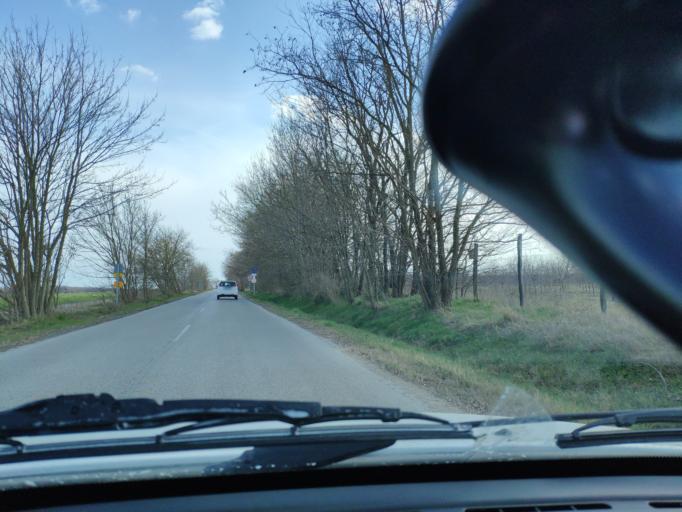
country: HU
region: Pest
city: Rackeve
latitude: 47.1478
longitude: 18.9096
